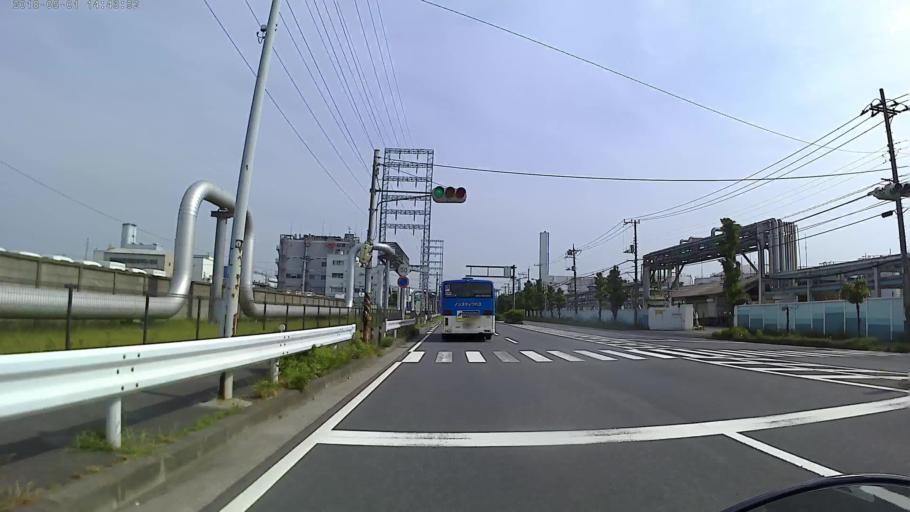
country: JP
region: Kanagawa
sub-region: Kawasaki-shi
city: Kawasaki
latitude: 35.5179
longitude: 139.7573
